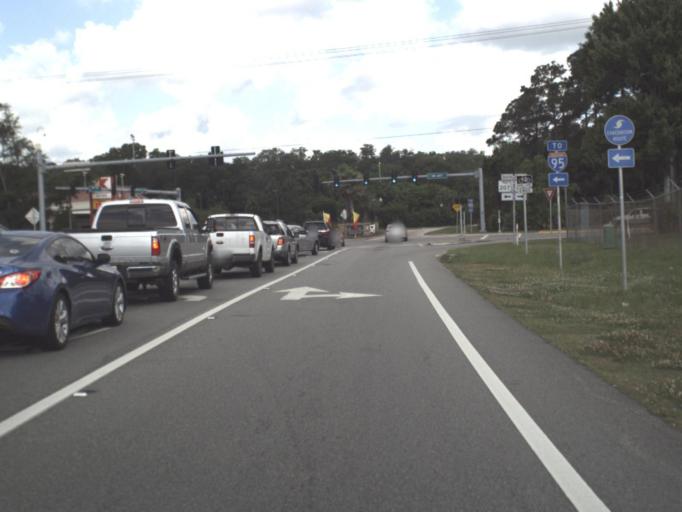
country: US
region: Florida
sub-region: Saint Johns County
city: Saint Augustine South
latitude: 29.8674
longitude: -81.3387
